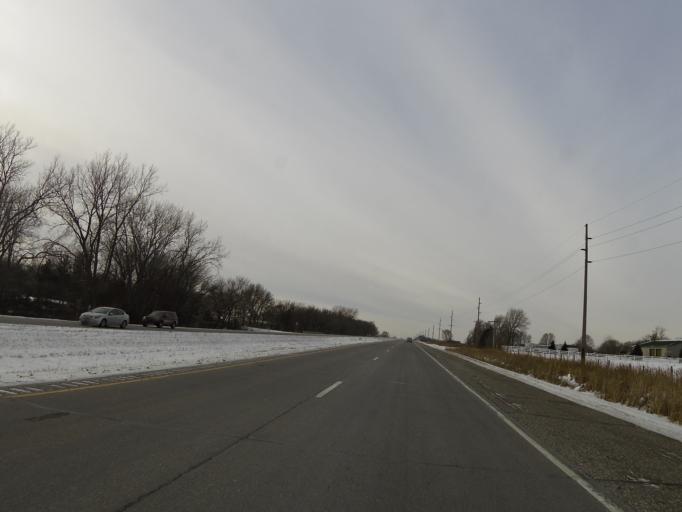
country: US
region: Minnesota
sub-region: Scott County
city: Belle Plaine
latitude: 44.6410
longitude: -93.7156
